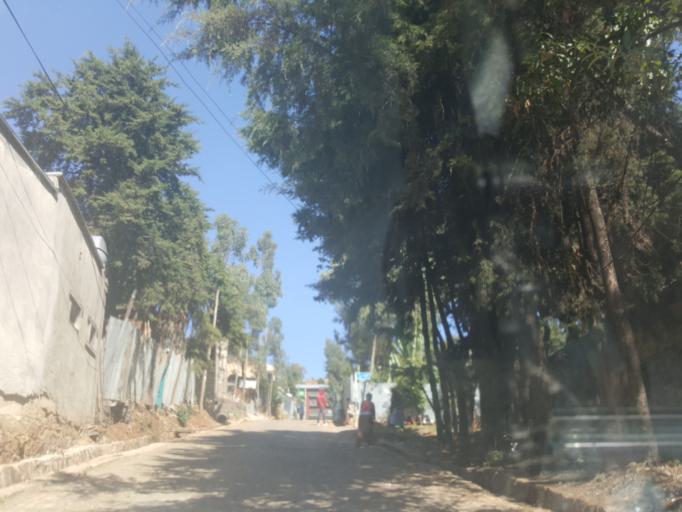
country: ET
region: Adis Abeba
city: Addis Ababa
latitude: 9.0698
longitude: 38.7331
